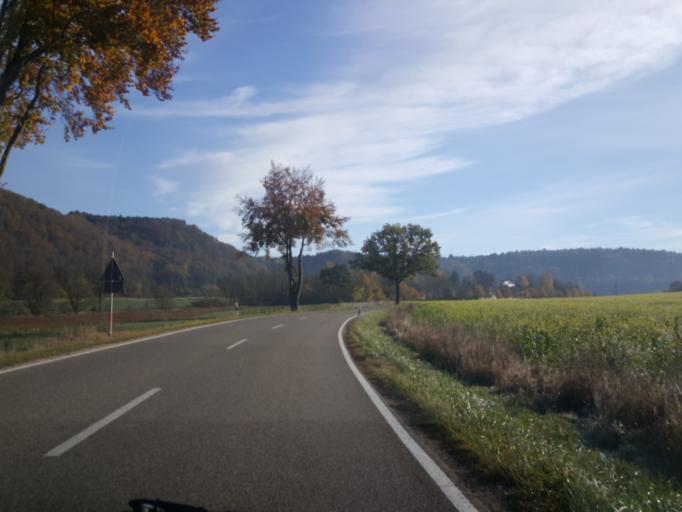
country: DE
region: Bavaria
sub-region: Upper Bavaria
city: Rennertshofen
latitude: 48.8115
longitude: 11.1158
